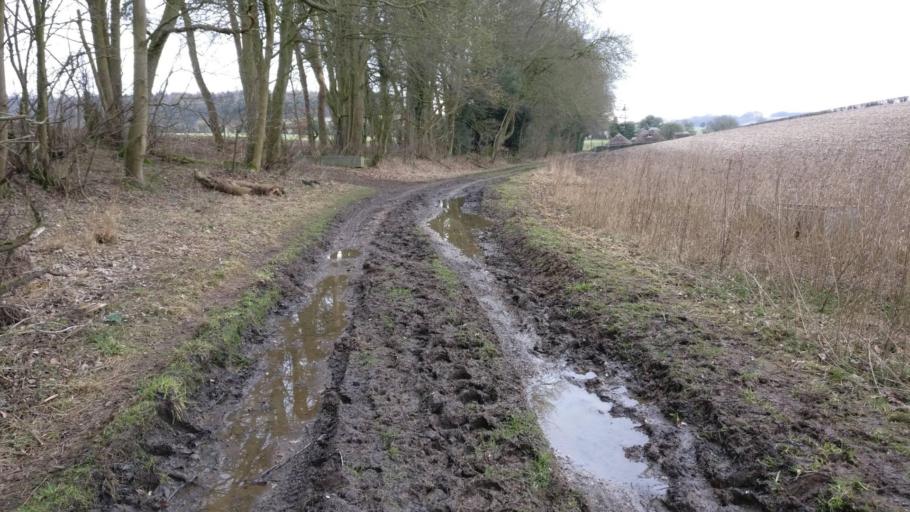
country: GB
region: England
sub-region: Hampshire
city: Basingstoke
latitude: 51.1922
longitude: -1.1138
